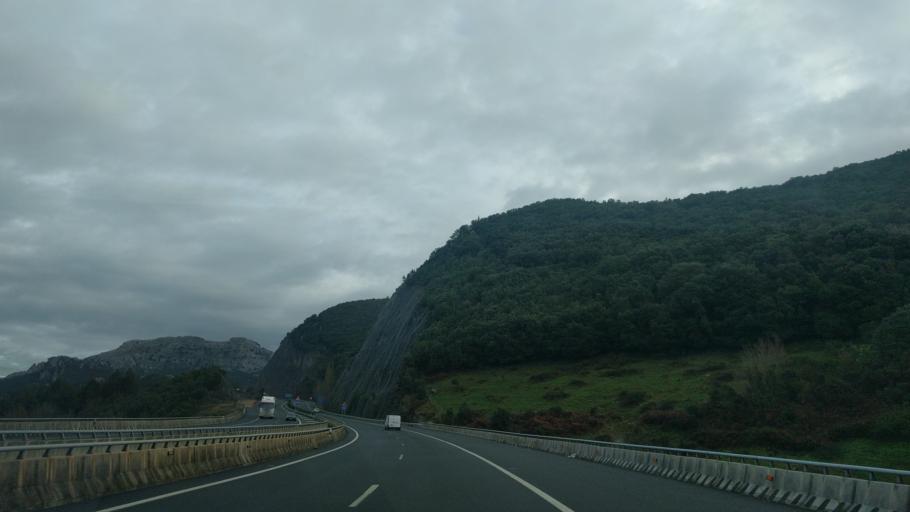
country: ES
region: Cantabria
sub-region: Provincia de Cantabria
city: Liendo
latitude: 43.3820
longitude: -3.3670
